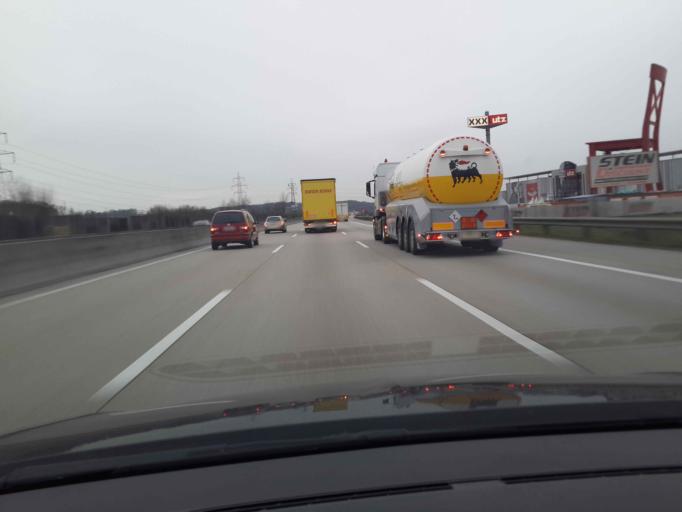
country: AT
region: Upper Austria
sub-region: Politischer Bezirk Linz-Land
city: Asten
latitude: 48.2225
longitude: 14.3967
